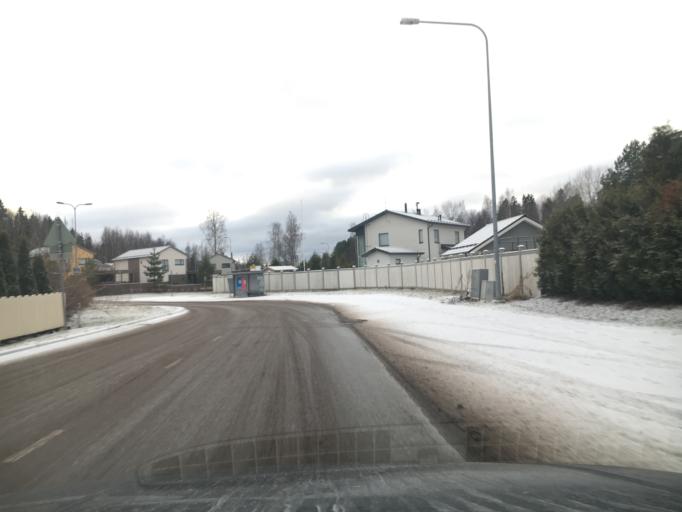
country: FI
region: Uusimaa
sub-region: Helsinki
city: Espoo
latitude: 60.1615
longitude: 24.6468
